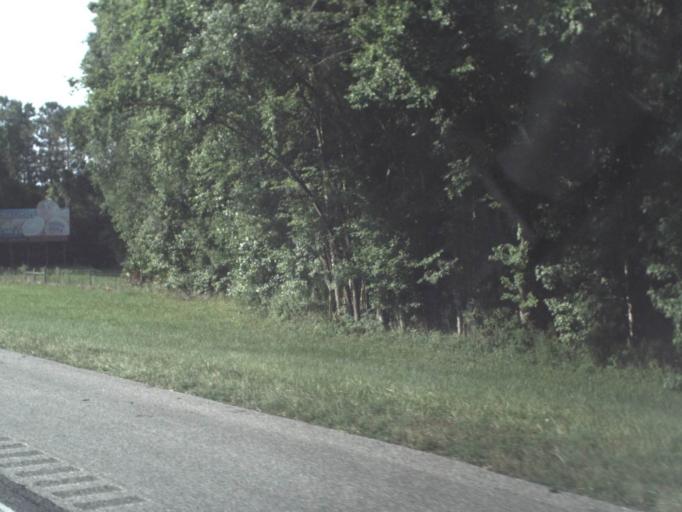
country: US
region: Florida
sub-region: Saint Johns County
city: Fruit Cove
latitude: 30.0277
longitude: -81.4867
